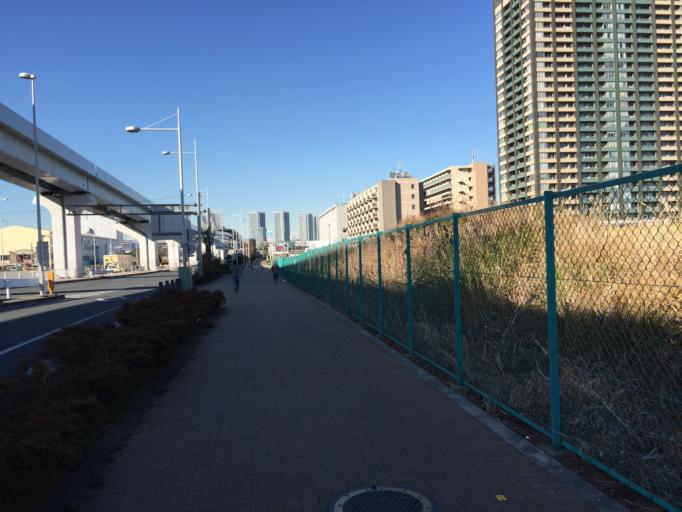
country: JP
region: Tokyo
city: Urayasu
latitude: 35.6371
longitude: 139.7915
